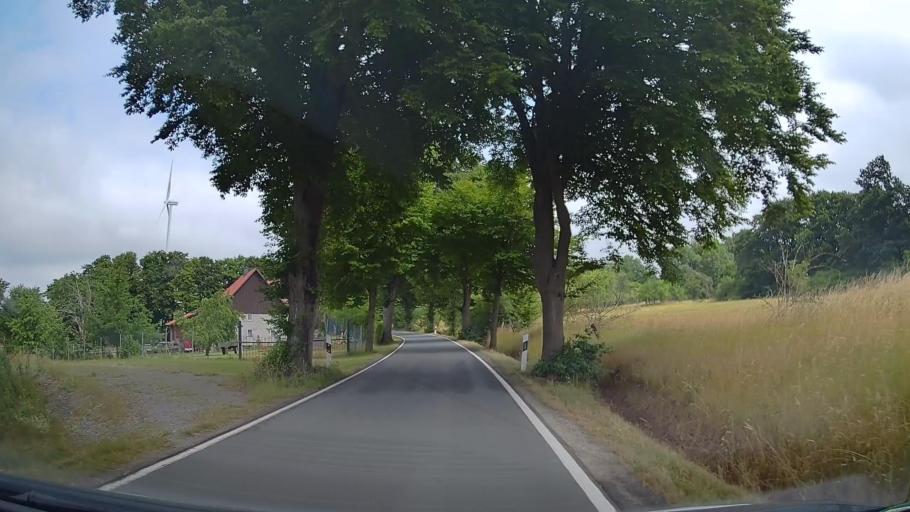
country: DE
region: North Rhine-Westphalia
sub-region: Regierungsbezirk Detmold
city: Barntrup
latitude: 52.0792
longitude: 9.1333
